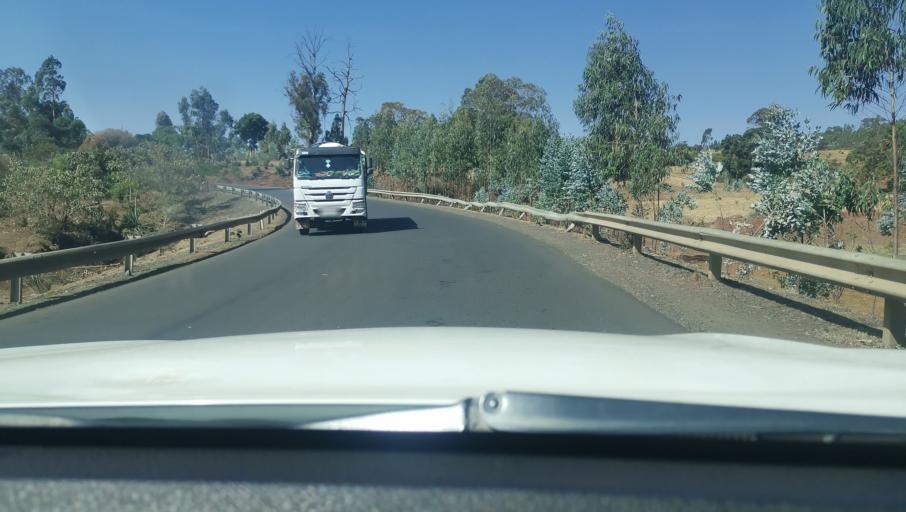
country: ET
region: Oromiya
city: Gedo
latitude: 8.9709
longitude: 37.5039
